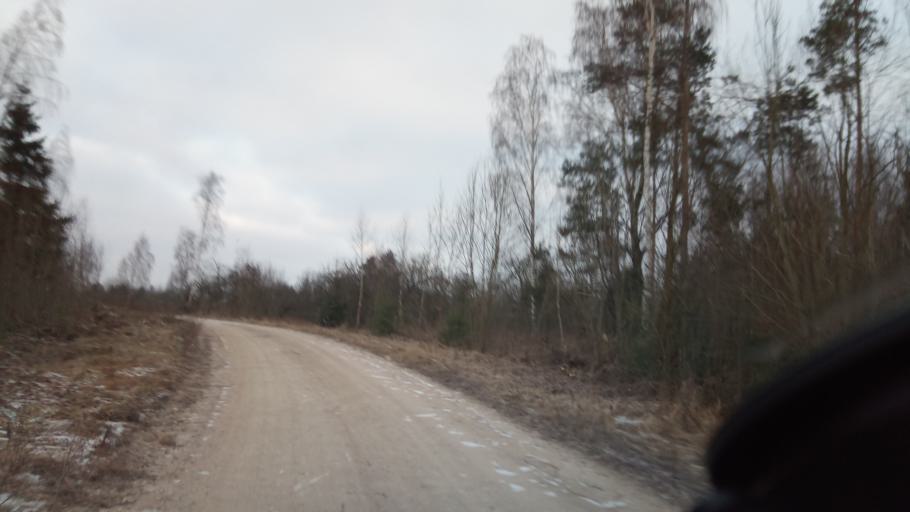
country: LT
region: Alytaus apskritis
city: Varena
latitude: 54.3687
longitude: 24.5459
